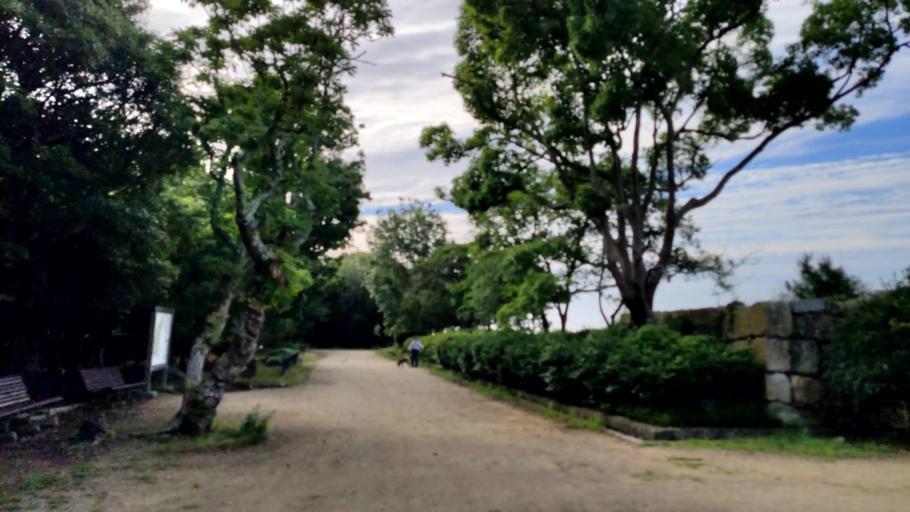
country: JP
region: Hyogo
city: Akashi
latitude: 34.6524
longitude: 134.9928
